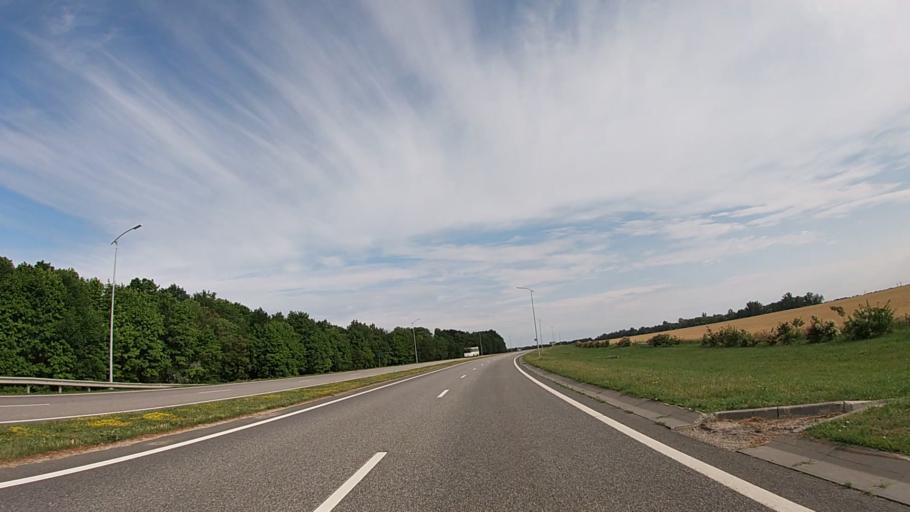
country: RU
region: Belgorod
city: Borisovka
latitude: 50.7559
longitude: 35.9658
